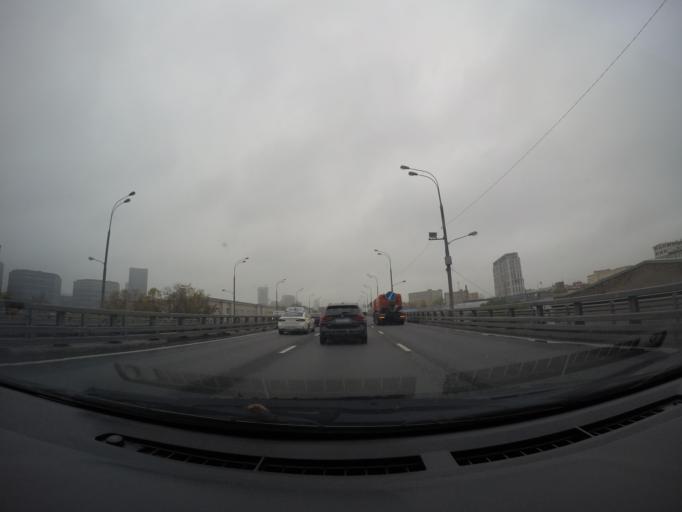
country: RU
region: Moskovskaya
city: Presnenskiy
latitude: 55.7679
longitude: 37.5236
